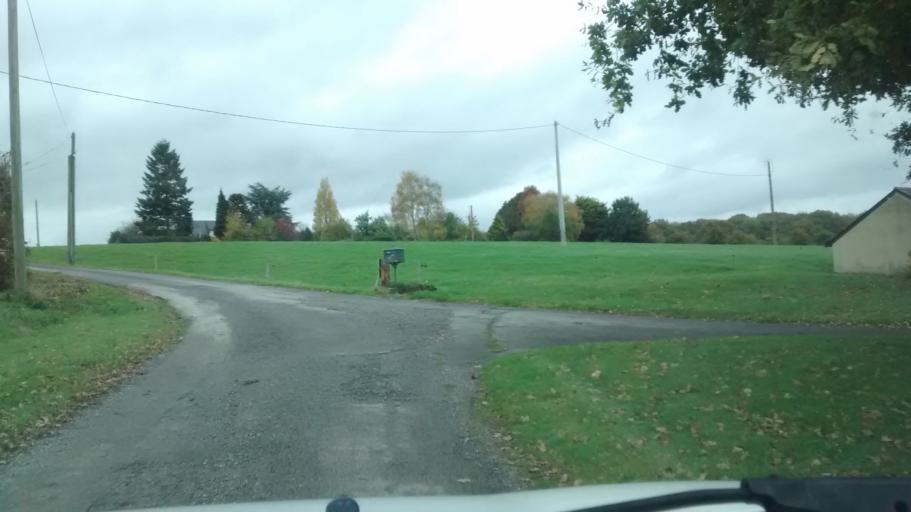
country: FR
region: Brittany
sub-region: Departement d'Ille-et-Vilaine
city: Servon-sur-Vilaine
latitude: 48.1350
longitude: -1.4504
